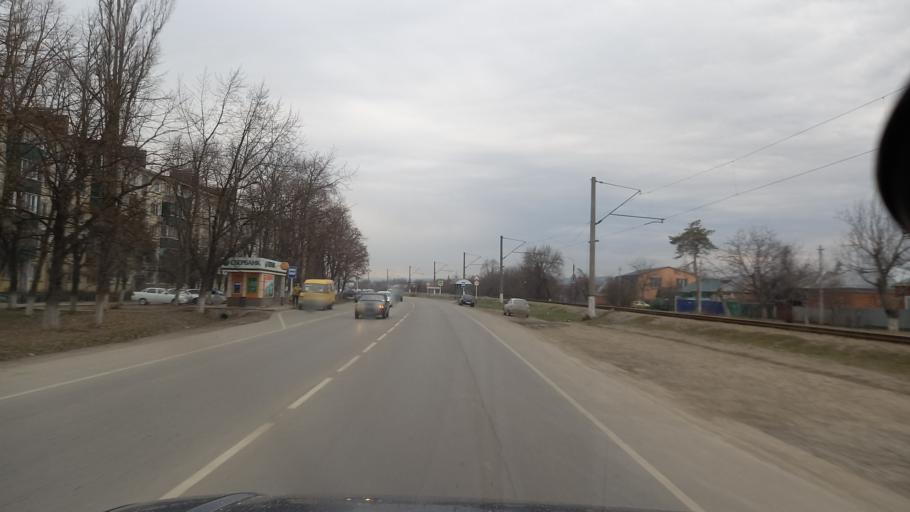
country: RU
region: Adygeya
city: Maykop
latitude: 44.5931
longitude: 40.1312
